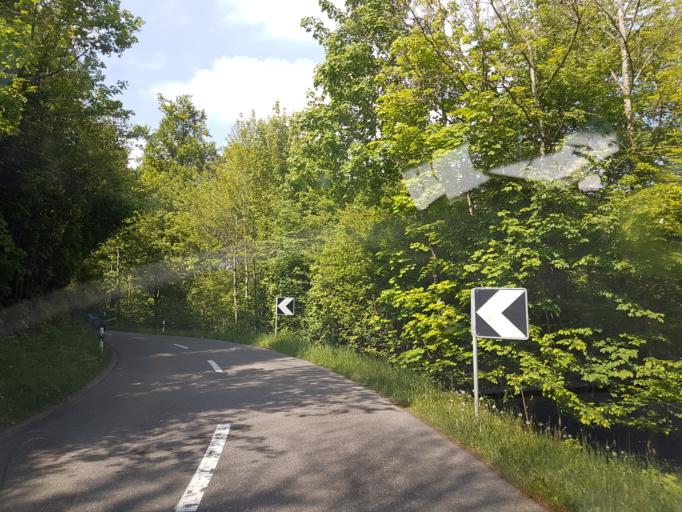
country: CH
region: Aargau
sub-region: Bezirk Bremgarten
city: Rudolfstetten
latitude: 47.3761
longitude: 8.3791
